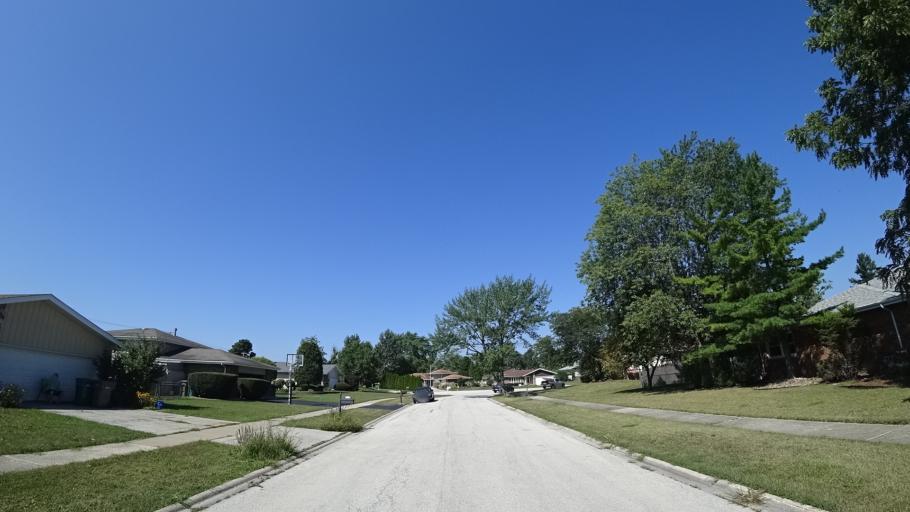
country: US
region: Illinois
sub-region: Cook County
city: Orland Park
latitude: 41.6316
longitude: -87.8243
